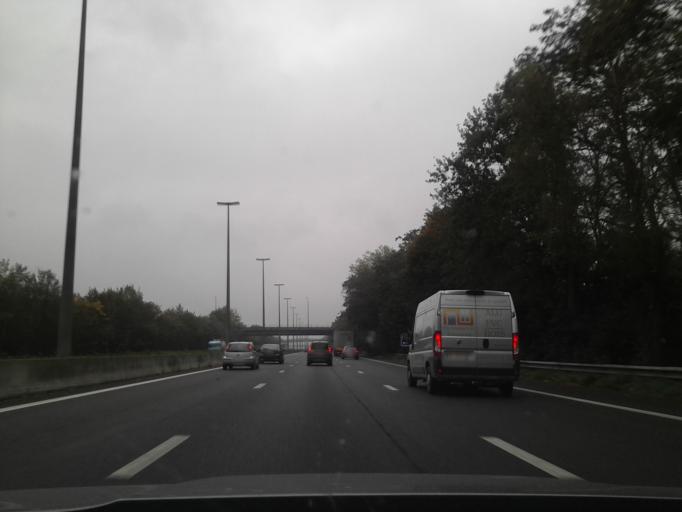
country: BE
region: Wallonia
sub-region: Province du Hainaut
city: Quaregnon
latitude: 50.4533
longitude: 3.8614
